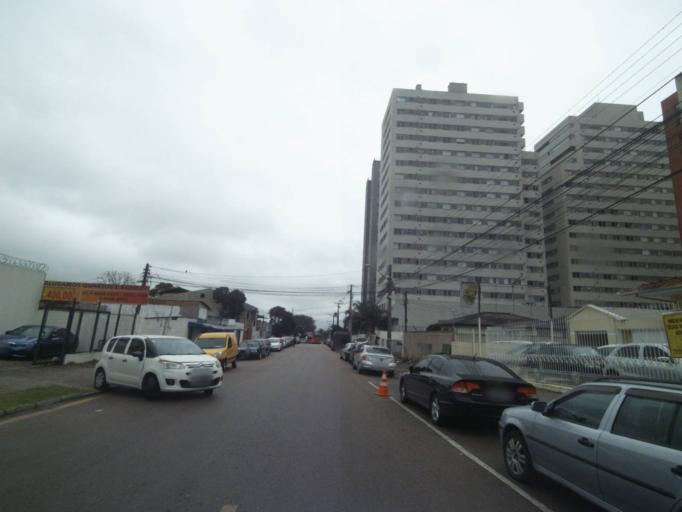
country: BR
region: Parana
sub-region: Sao Jose Dos Pinhais
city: Sao Jose dos Pinhais
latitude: -25.5143
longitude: -49.2959
